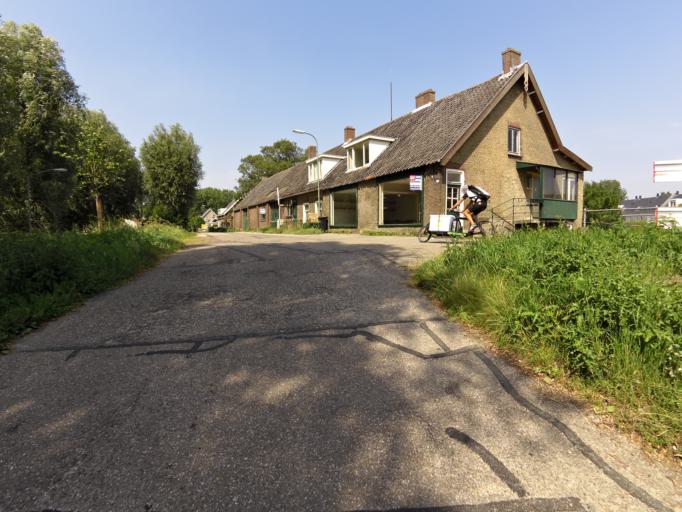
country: NL
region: South Holland
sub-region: Gemeente Dordrecht
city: Dordrecht
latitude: 51.7847
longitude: 4.6634
